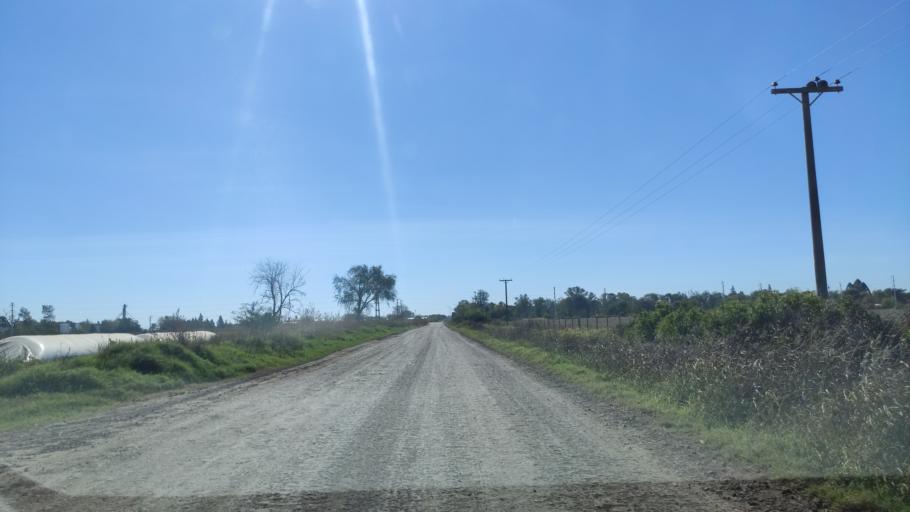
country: AR
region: Cordoba
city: Leones
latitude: -32.6660
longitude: -62.3118
